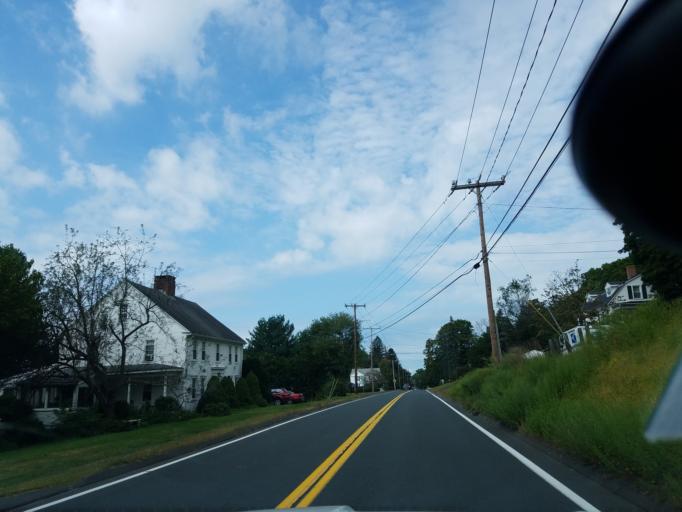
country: US
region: Connecticut
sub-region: Hartford County
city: Wethersfield
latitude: 41.6748
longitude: -72.6428
